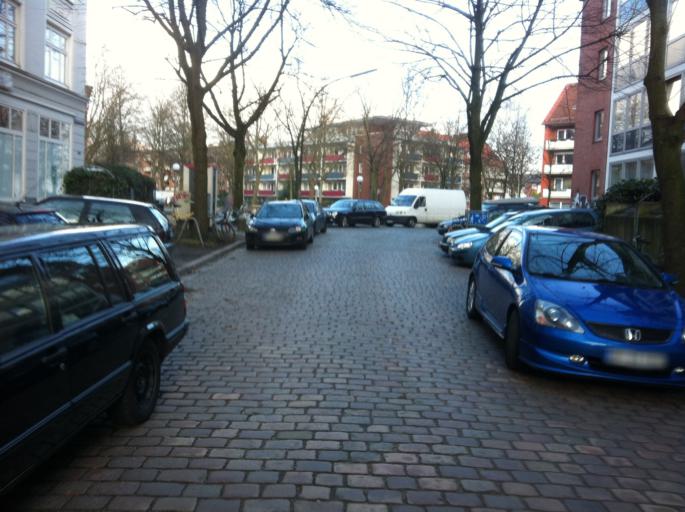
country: DE
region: Hamburg
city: St. Pauli
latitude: 53.5660
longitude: 9.9468
